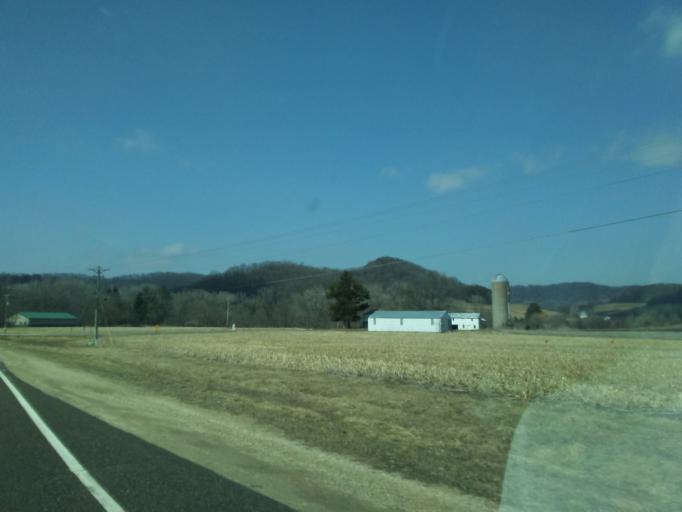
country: US
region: Wisconsin
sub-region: La Crosse County
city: La Crosse
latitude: 43.7632
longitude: -91.1396
